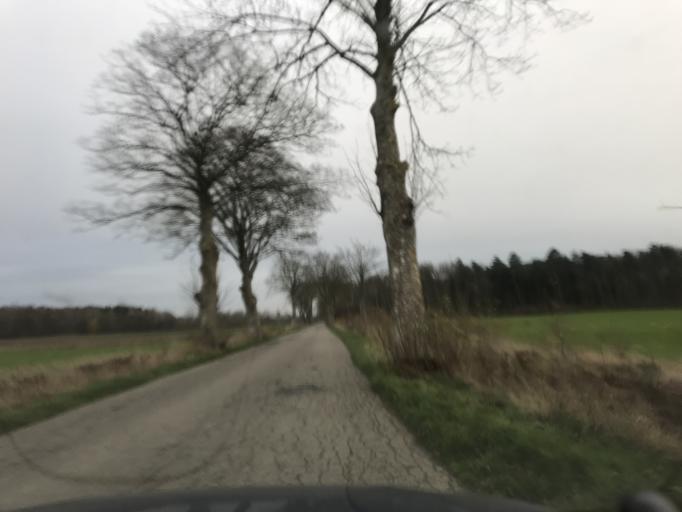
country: PL
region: Pomeranian Voivodeship
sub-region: Powiat slupski
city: Kobylnica
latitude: 54.4387
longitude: 16.8934
